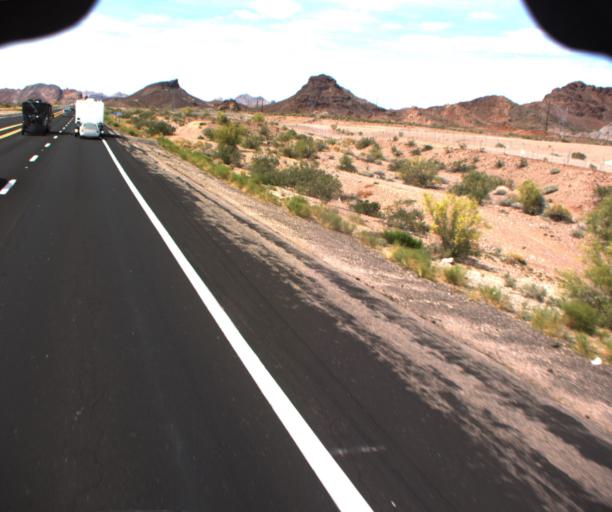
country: US
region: Arizona
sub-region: Mohave County
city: Desert Hills
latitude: 34.5798
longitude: -114.3671
